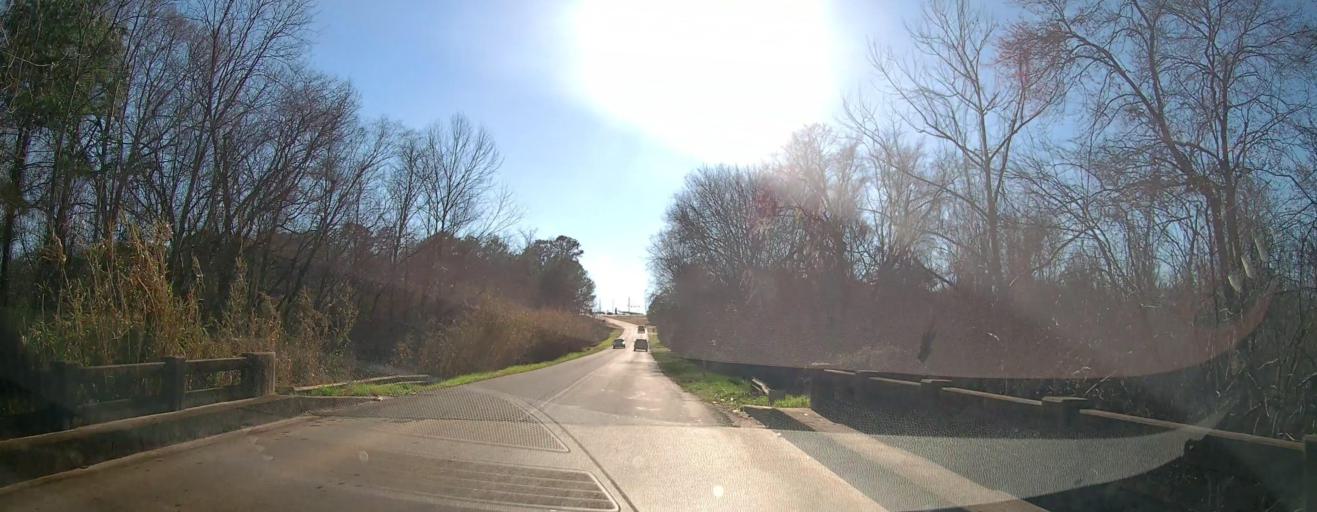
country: US
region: Georgia
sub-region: Sumter County
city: Americus
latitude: 32.0679
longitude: -84.2478
